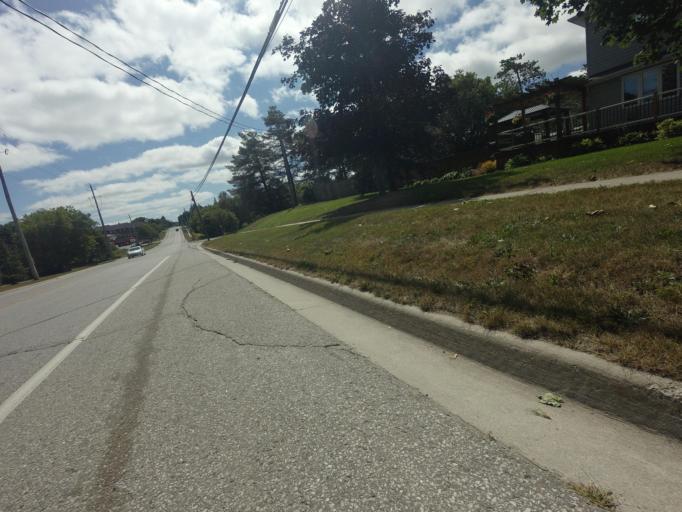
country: CA
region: Ontario
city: Uxbridge
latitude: 44.1201
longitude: -79.1253
